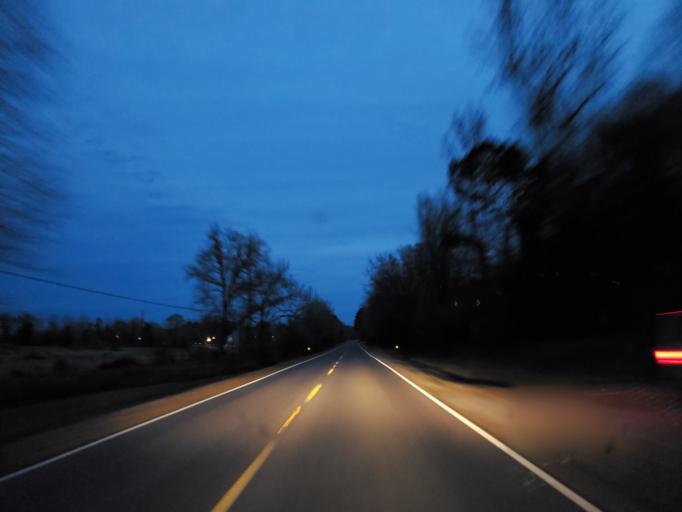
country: US
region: Alabama
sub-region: Greene County
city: Eutaw
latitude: 32.8820
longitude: -87.9366
